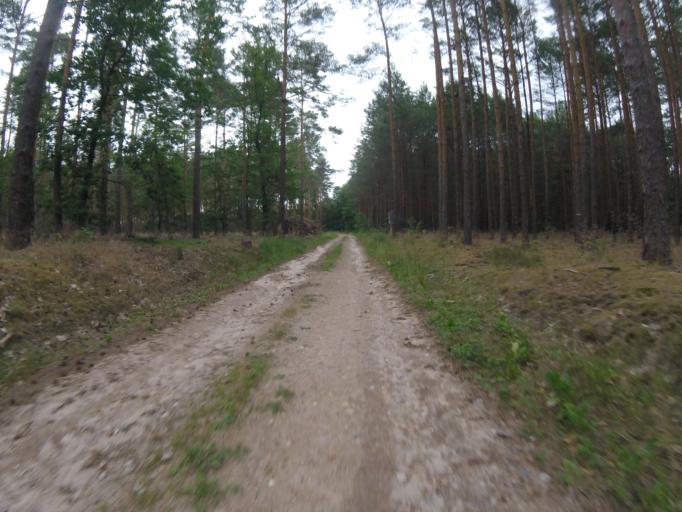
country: DE
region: Brandenburg
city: Gross Koris
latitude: 52.2123
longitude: 13.6864
